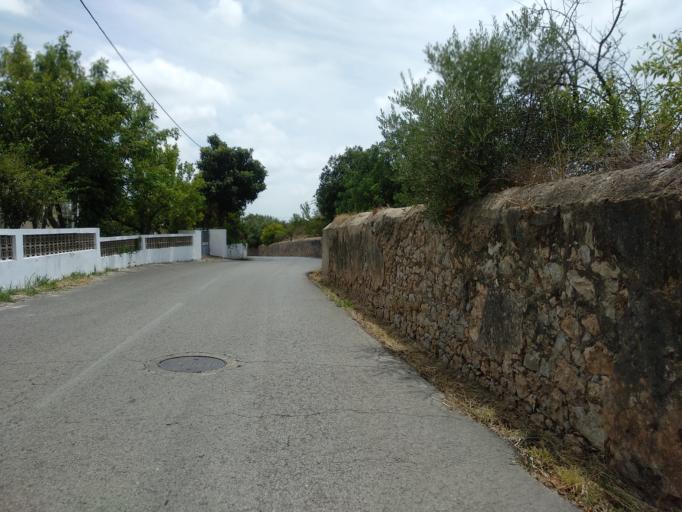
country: PT
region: Faro
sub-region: Sao Bras de Alportel
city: Sao Bras de Alportel
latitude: 37.1607
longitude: -7.8851
